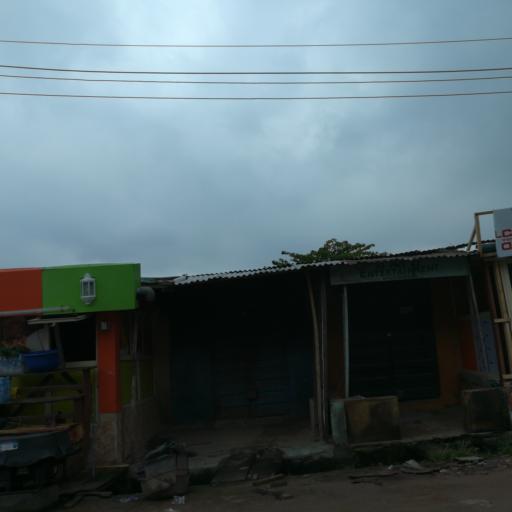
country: NG
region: Lagos
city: Agege
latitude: 6.6007
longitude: 3.3003
